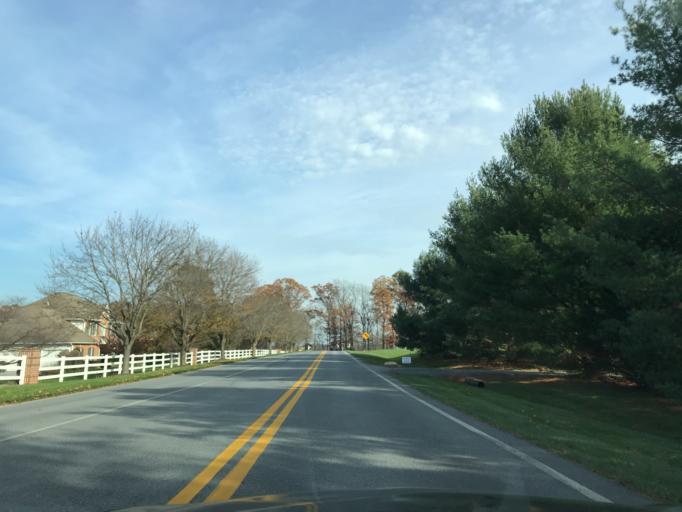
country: US
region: Maryland
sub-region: Baltimore County
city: Reisterstown
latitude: 39.4947
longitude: -76.9140
